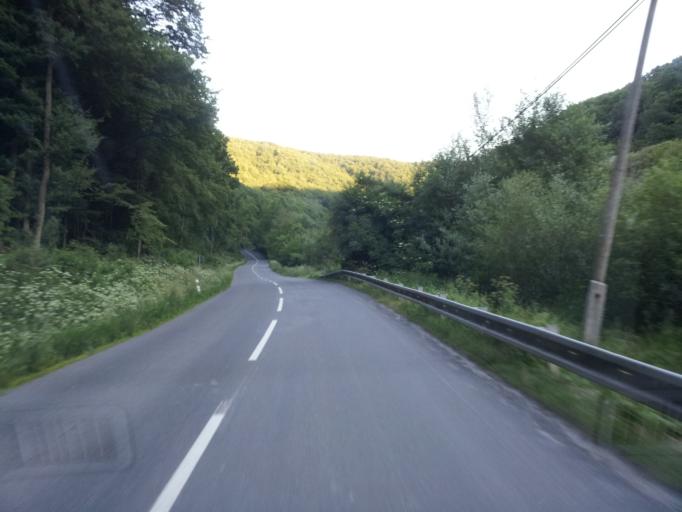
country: SK
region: Banskobystricky
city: Krupina
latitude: 48.3195
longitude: 18.9778
